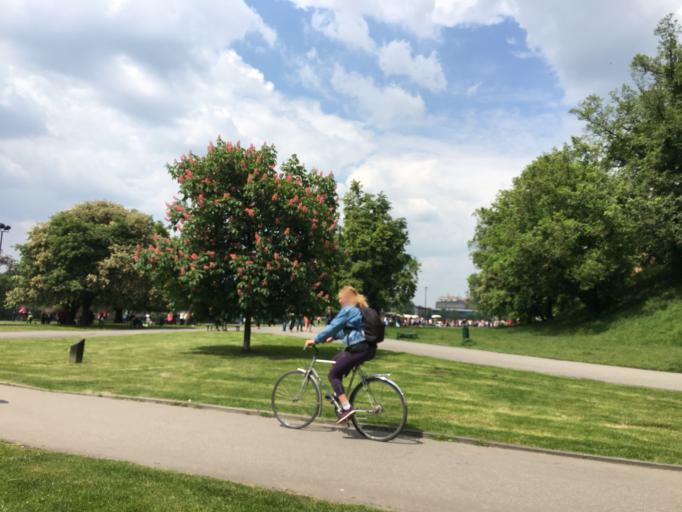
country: PL
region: Lesser Poland Voivodeship
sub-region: Krakow
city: Krakow
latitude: 50.0524
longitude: 19.9348
